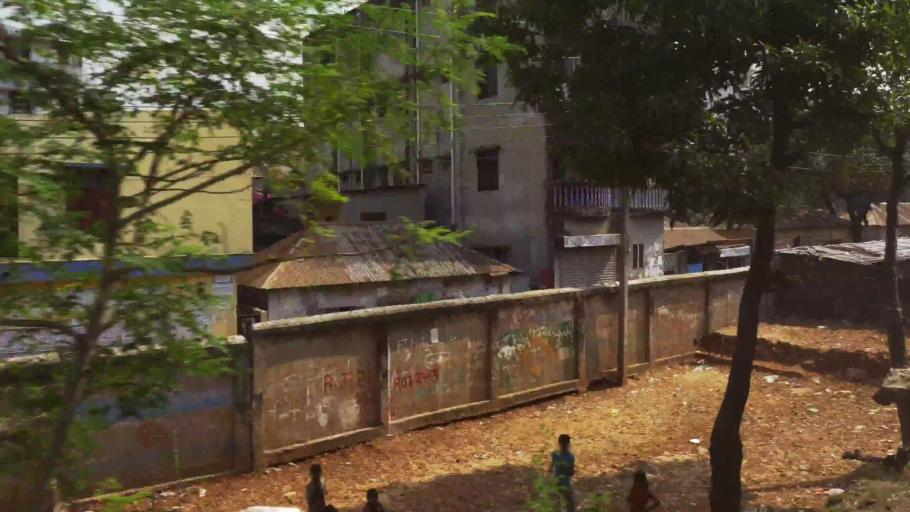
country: BD
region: Dhaka
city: Paltan
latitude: 23.8092
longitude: 90.4029
